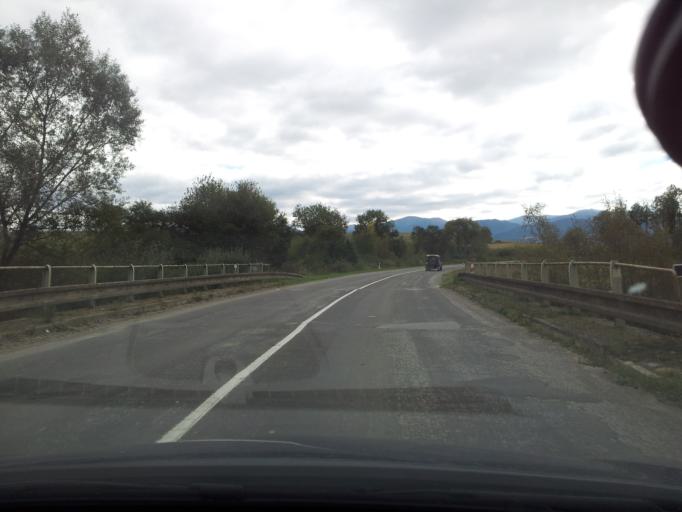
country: SK
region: Zilinsky
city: Ruzomberok
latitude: 49.0850
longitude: 19.4386
